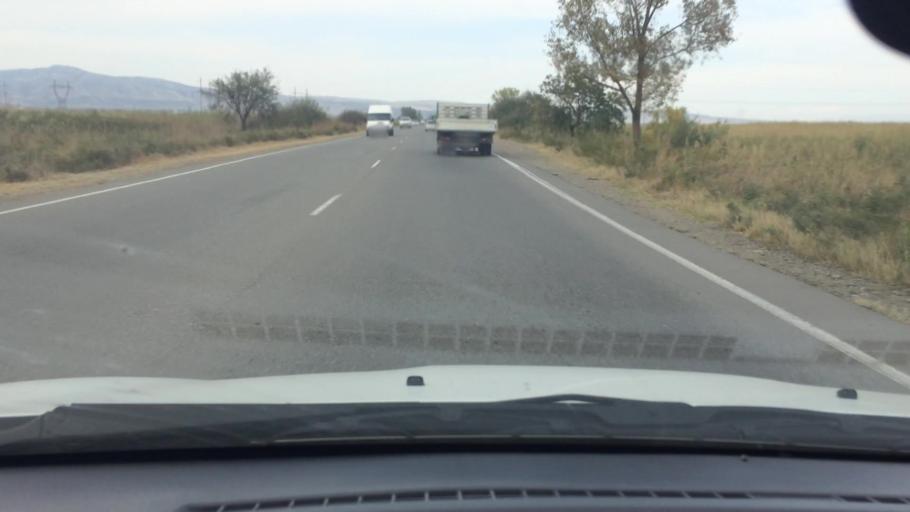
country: GE
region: Kvemo Kartli
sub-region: Marneuli
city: Marneuli
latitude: 41.5393
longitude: 44.7769
